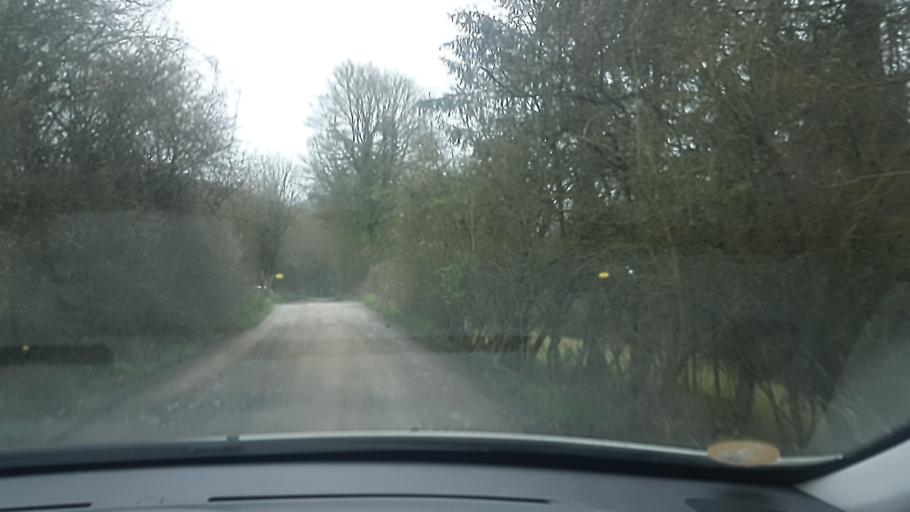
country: BE
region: Wallonia
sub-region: Province de Namur
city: Couvin
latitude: 50.0762
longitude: 4.5955
